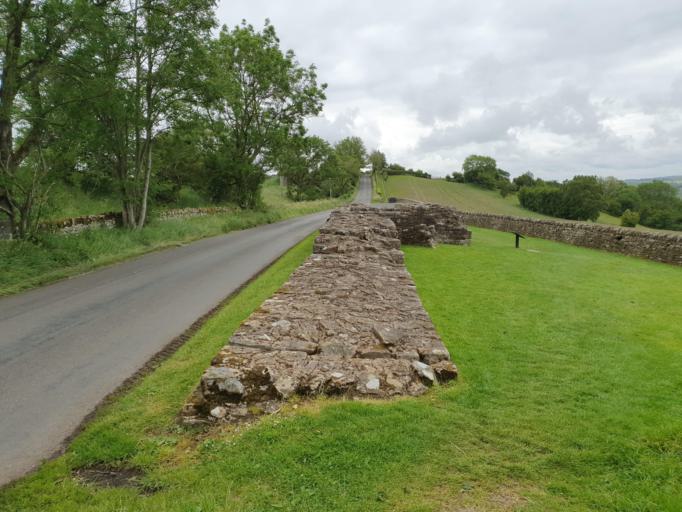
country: GB
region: England
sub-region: Cumbria
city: Brampton
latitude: 54.9752
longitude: -2.6664
